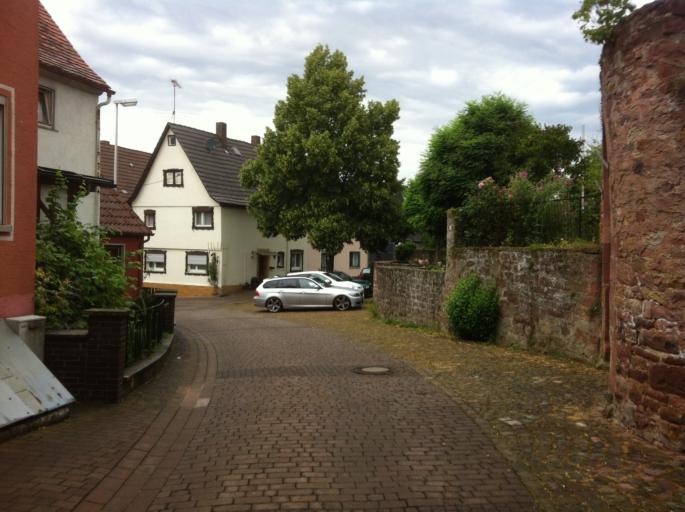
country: DE
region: Bavaria
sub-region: Regierungsbezirk Unterfranken
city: Eschau
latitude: 49.8194
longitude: 9.2560
